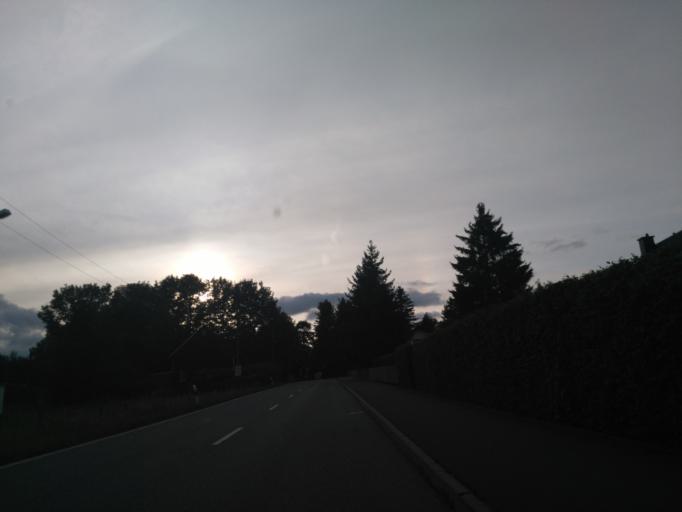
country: DE
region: Saxony
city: Geyer
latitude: 50.6260
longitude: 12.9325
